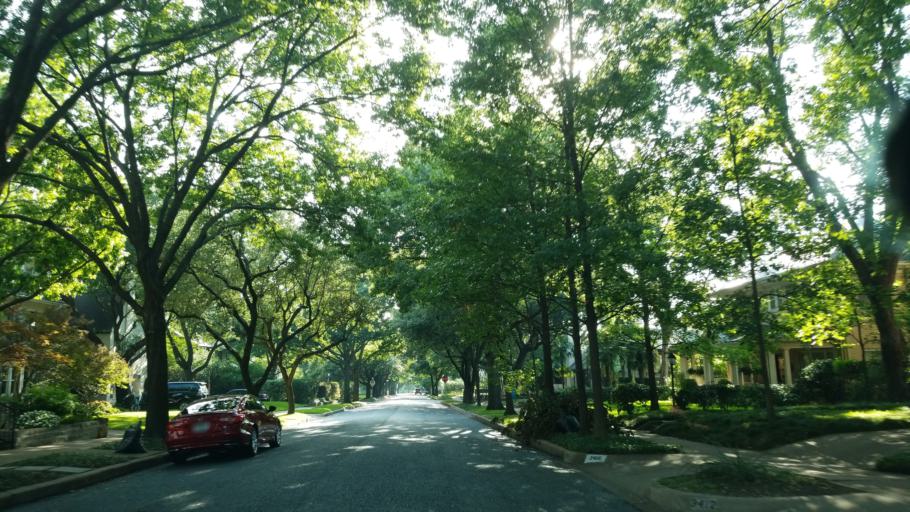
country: US
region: Texas
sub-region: Dallas County
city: Highland Park
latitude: 32.8335
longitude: -96.7880
